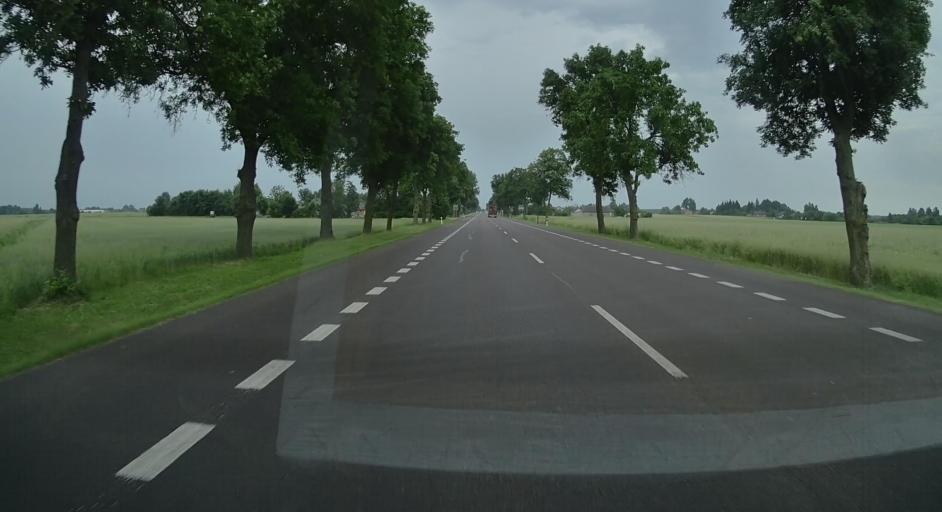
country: PL
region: Lublin Voivodeship
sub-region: Powiat bialski
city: Rzeczyca
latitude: 52.0395
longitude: 22.6906
